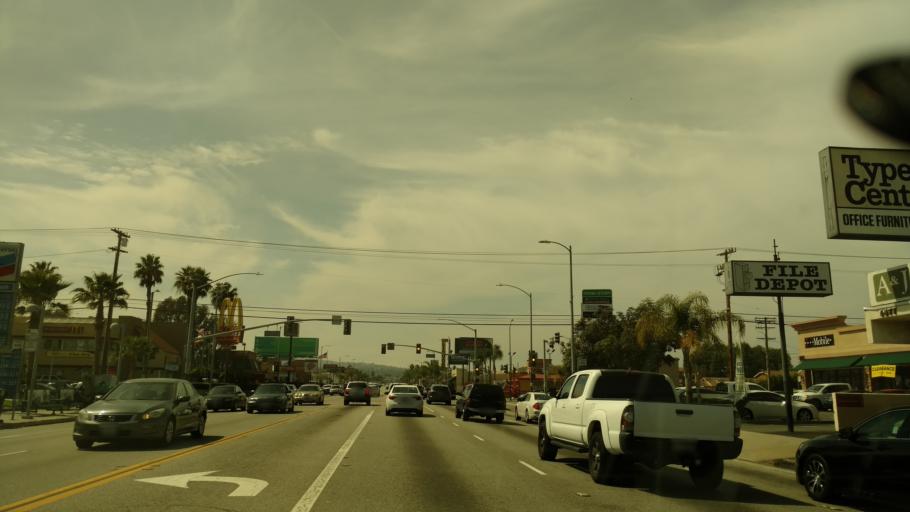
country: US
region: California
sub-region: Los Angeles County
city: Lomita
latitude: 33.7895
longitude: -118.3067
